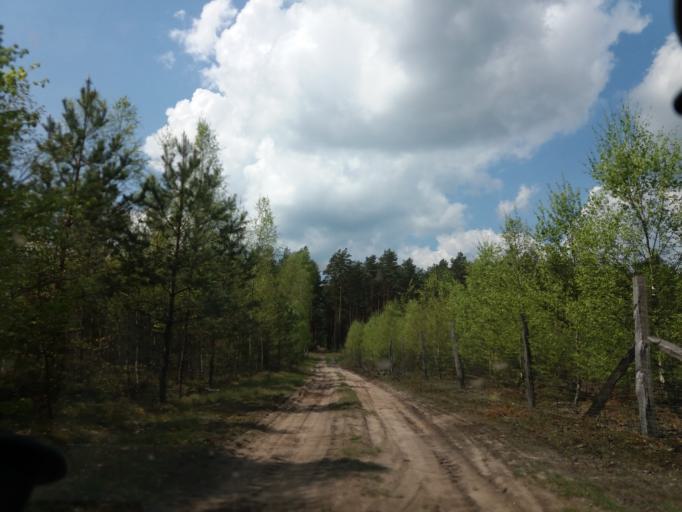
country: PL
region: West Pomeranian Voivodeship
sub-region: Powiat walecki
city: Czlopa
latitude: 53.1070
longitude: 15.9538
